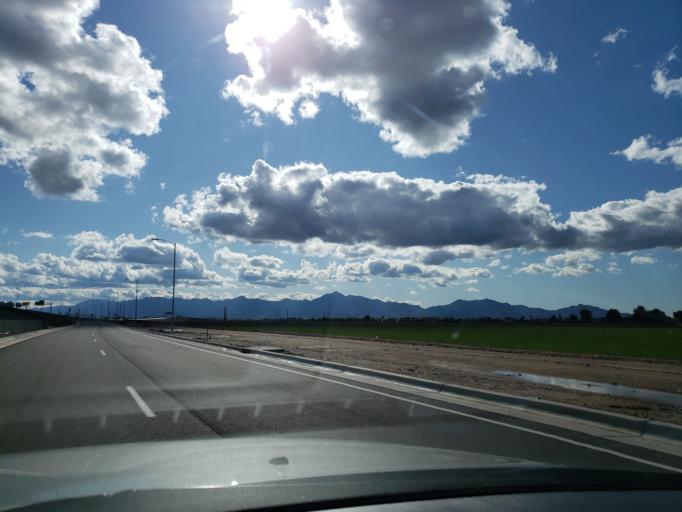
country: US
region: Arizona
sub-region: Maricopa County
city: Laveen
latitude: 33.4323
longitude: -112.1879
